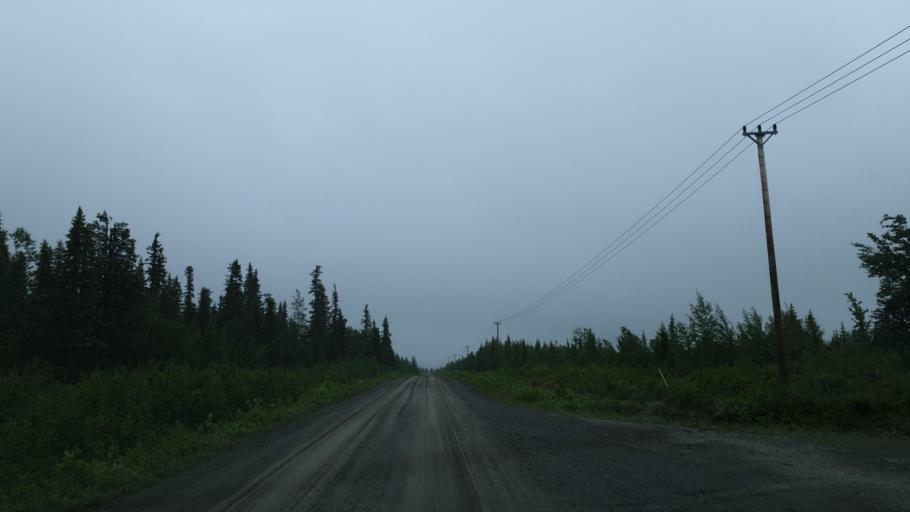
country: SE
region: Vaesterbotten
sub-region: Vilhelmina Kommun
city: Sjoberg
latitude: 65.3157
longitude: 15.9556
